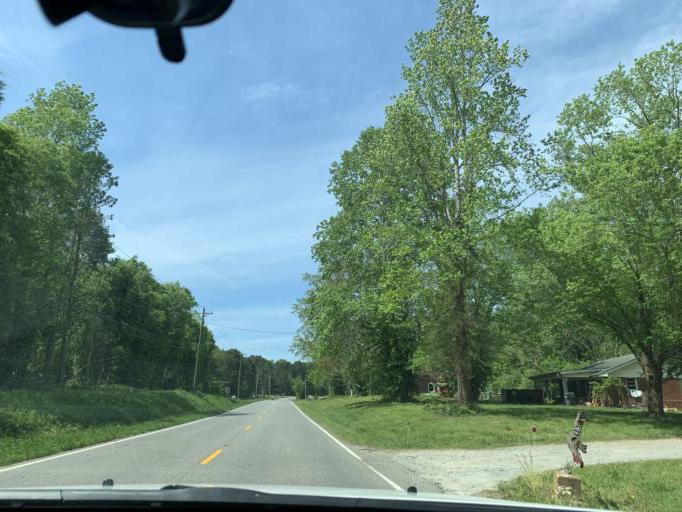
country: US
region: Georgia
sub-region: Forsyth County
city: Cumming
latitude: 34.2648
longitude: -84.1737
